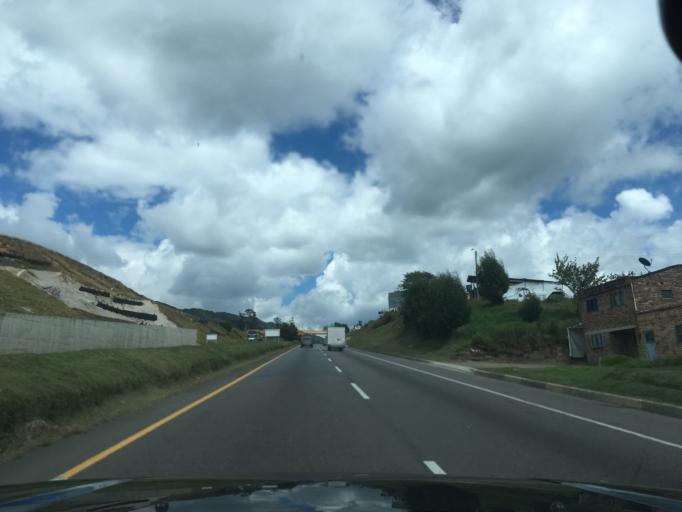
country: CO
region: Boyaca
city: Ventaquemada
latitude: 5.3890
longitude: -73.4994
